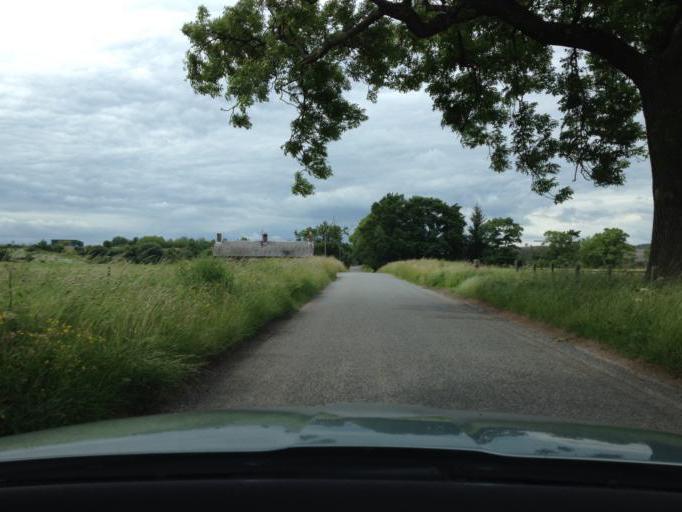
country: GB
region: Scotland
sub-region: Perth and Kinross
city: Bridge of Earn
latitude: 56.3341
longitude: -3.3937
